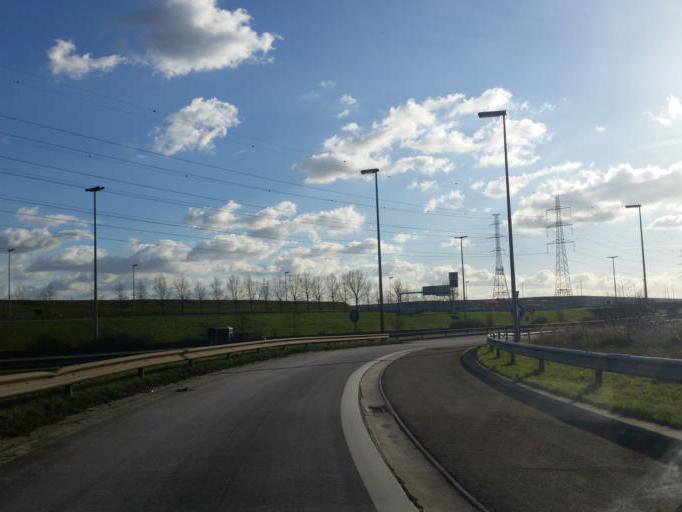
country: BE
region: Flanders
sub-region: Provincie Antwerpen
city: Zwijndrecht
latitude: 51.2817
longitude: 4.2845
